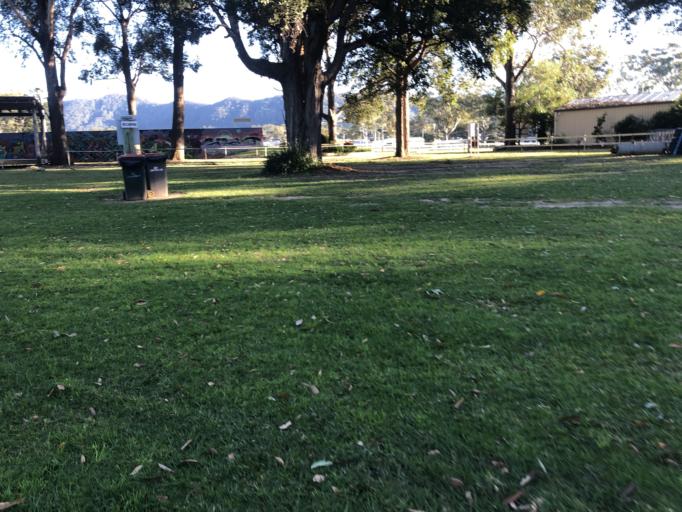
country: AU
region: New South Wales
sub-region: Coffs Harbour
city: Coffs Harbour
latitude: -30.2940
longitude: 153.1205
